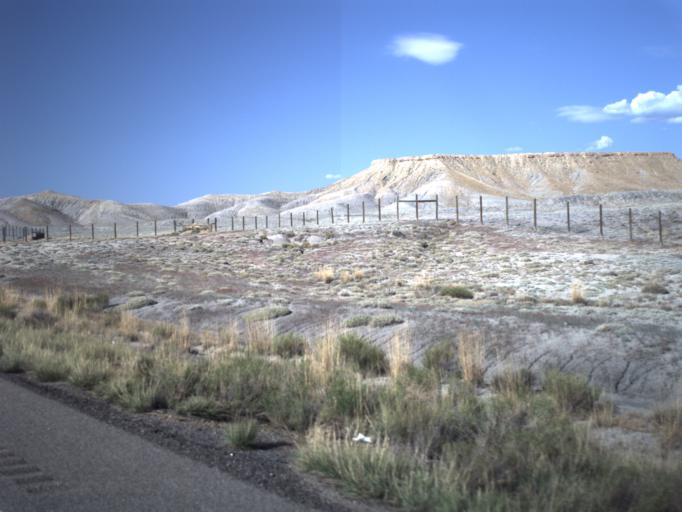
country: US
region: Utah
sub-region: Emery County
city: Huntington
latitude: 39.4234
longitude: -110.8708
